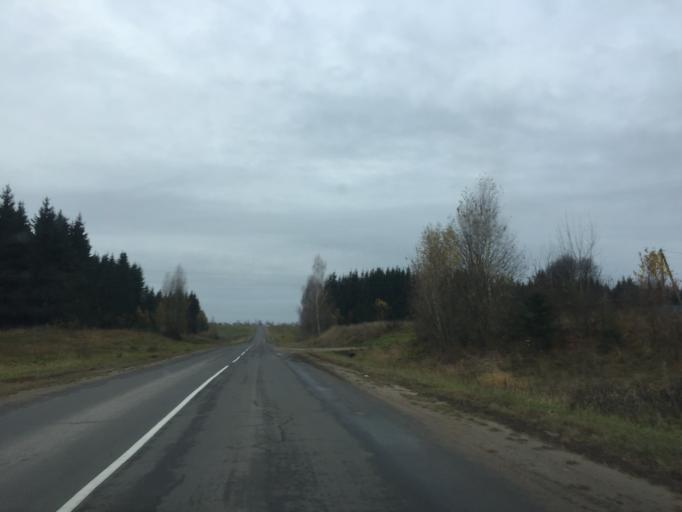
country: BY
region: Mogilev
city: Horki
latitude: 54.3129
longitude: 30.9536
